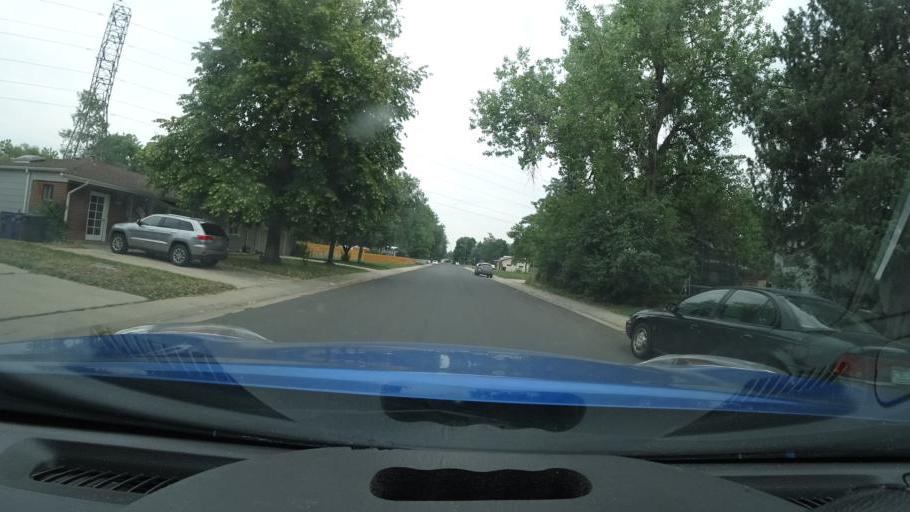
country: US
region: Colorado
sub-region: Arapahoe County
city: Glendale
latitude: 39.6929
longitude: -104.9184
